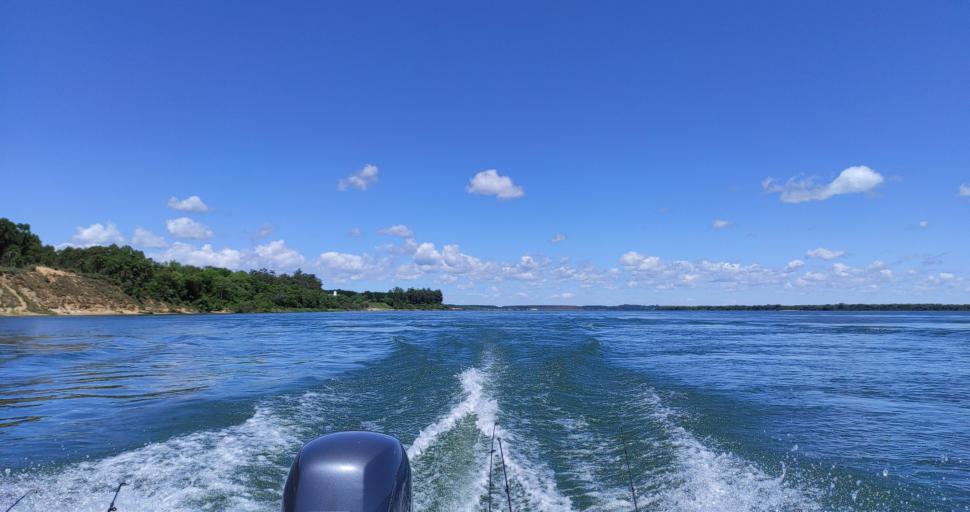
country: AR
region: Corrientes
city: Ituzaingo
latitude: -27.5891
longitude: -56.7955
